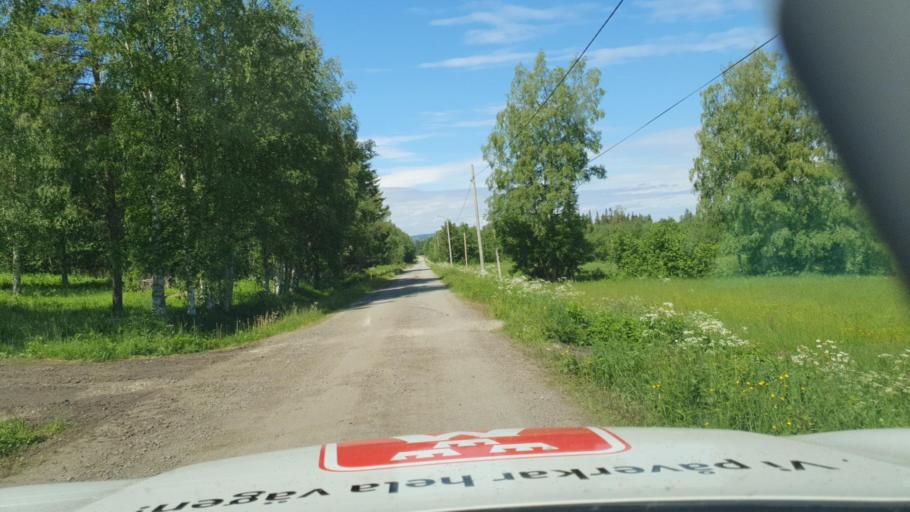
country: SE
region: Jaemtland
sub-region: Bergs Kommun
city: Hoverberg
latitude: 62.8419
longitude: 14.4376
